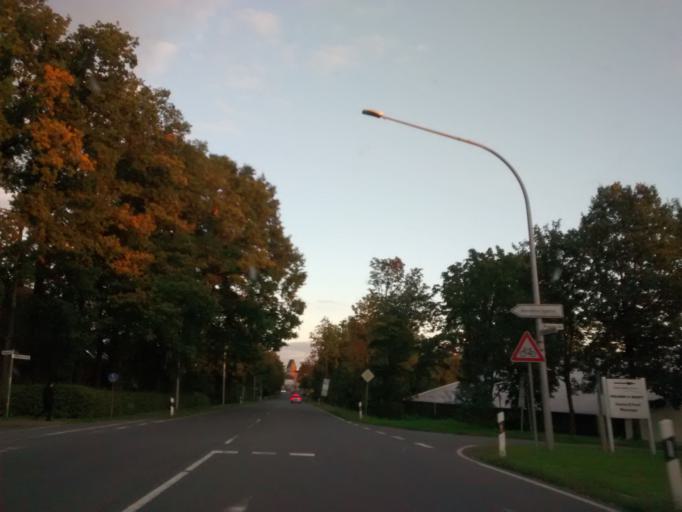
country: DE
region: North Rhine-Westphalia
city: Halle
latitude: 52.0651
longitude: 8.3524
